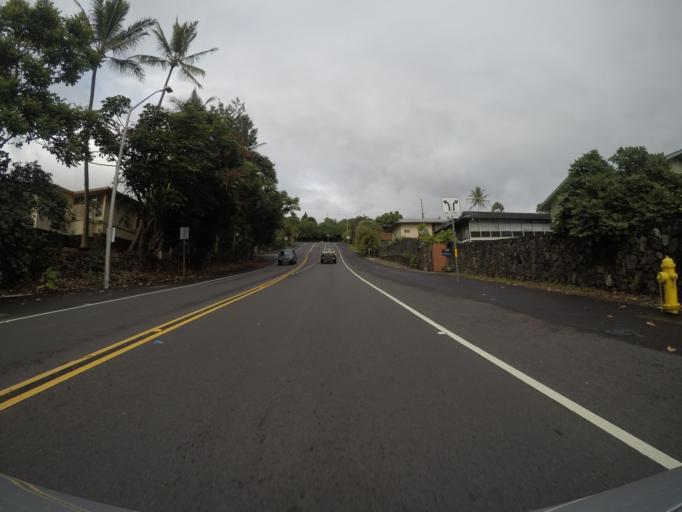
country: US
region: Hawaii
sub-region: Hawaii County
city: Kalaoa
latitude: 19.7176
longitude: -155.9789
